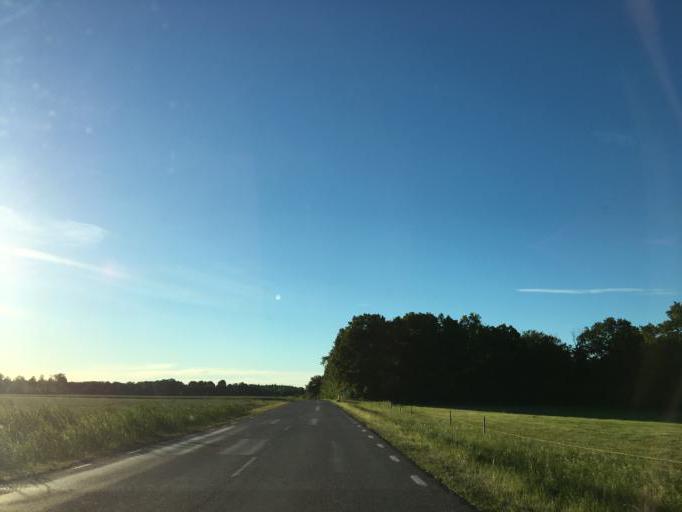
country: SE
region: Vaestmanland
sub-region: Vasteras
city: Vasteras
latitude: 59.5506
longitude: 16.5366
